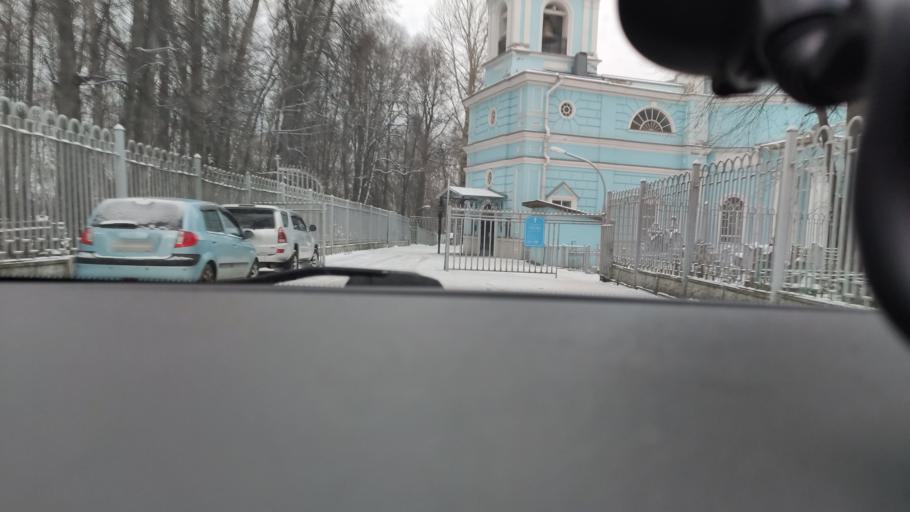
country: RU
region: Perm
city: Perm
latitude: 58.0107
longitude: 56.2655
